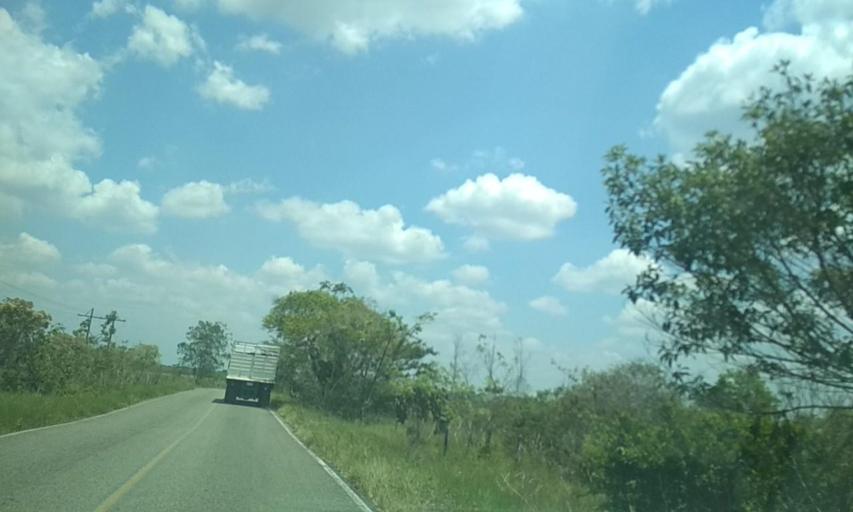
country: MX
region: Tabasco
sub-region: Huimanguillo
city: Francisco Rueda
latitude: 17.7684
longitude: -93.8010
